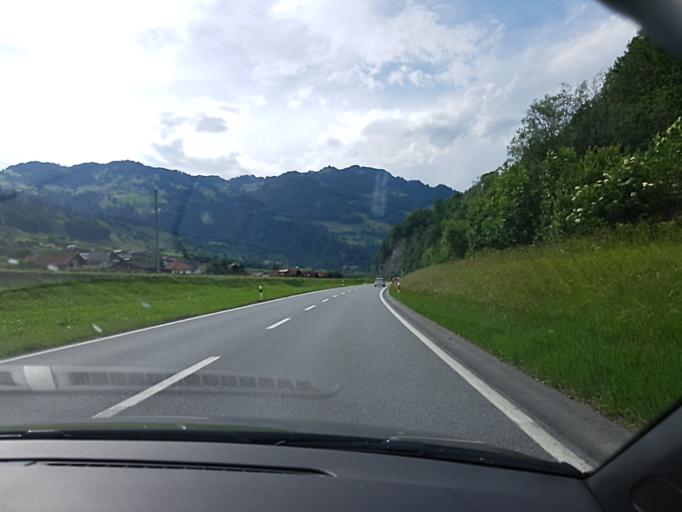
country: CH
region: Grisons
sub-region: Praettigau/Davos District
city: Jenaz
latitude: 46.9260
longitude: 9.7251
